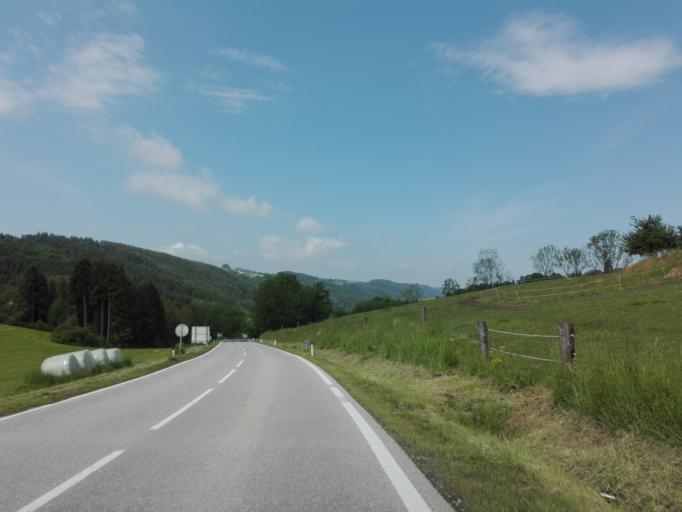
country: AT
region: Upper Austria
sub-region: Politischer Bezirk Rohrbach
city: Kleinzell im Muehlkreis
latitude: 48.3991
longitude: 13.9128
